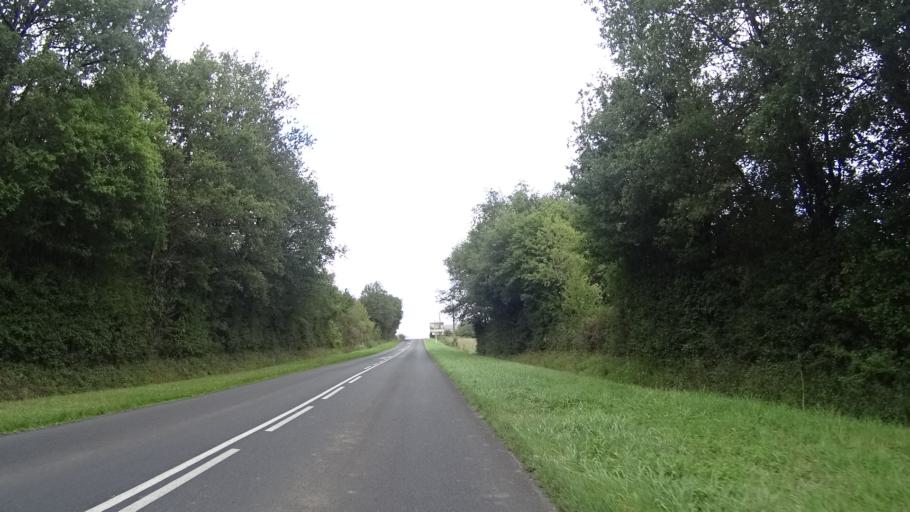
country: FR
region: Pays de la Loire
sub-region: Departement de Maine-et-Loire
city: Fontevraud-l'Abbaye
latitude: 47.1700
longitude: 0.0472
